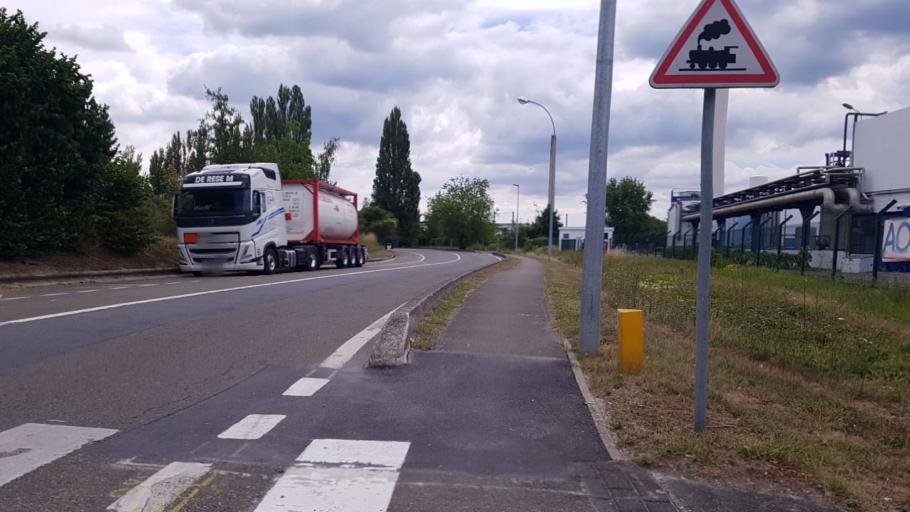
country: FR
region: Picardie
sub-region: Departement de l'Oise
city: Clairoix
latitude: 49.4335
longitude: 2.8520
